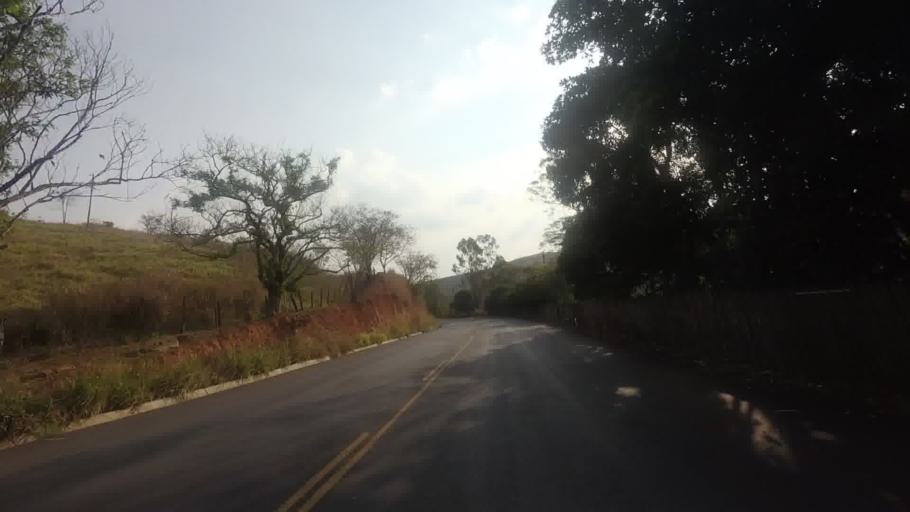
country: BR
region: Rio de Janeiro
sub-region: Itaperuna
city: Itaperuna
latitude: -21.3840
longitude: -41.9631
